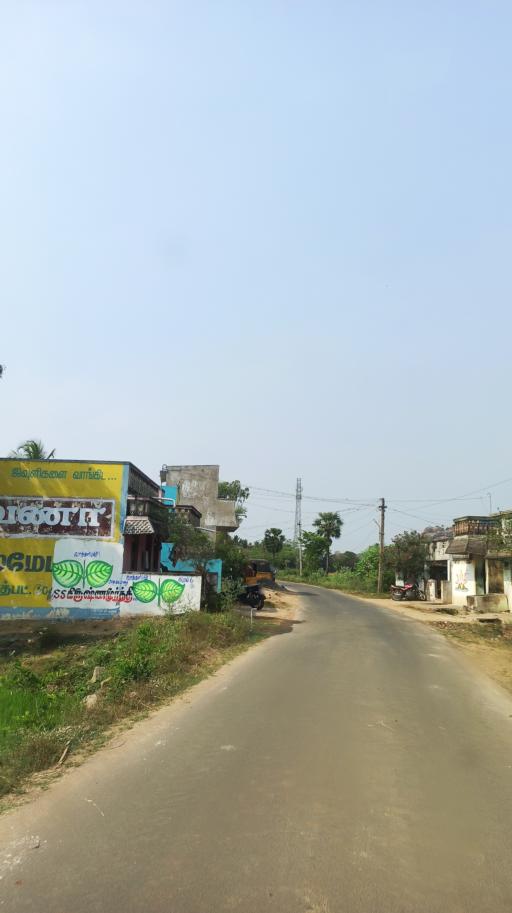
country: IN
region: Tamil Nadu
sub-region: Tiruvannamalai
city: Desur
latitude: 12.4514
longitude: 79.3723
